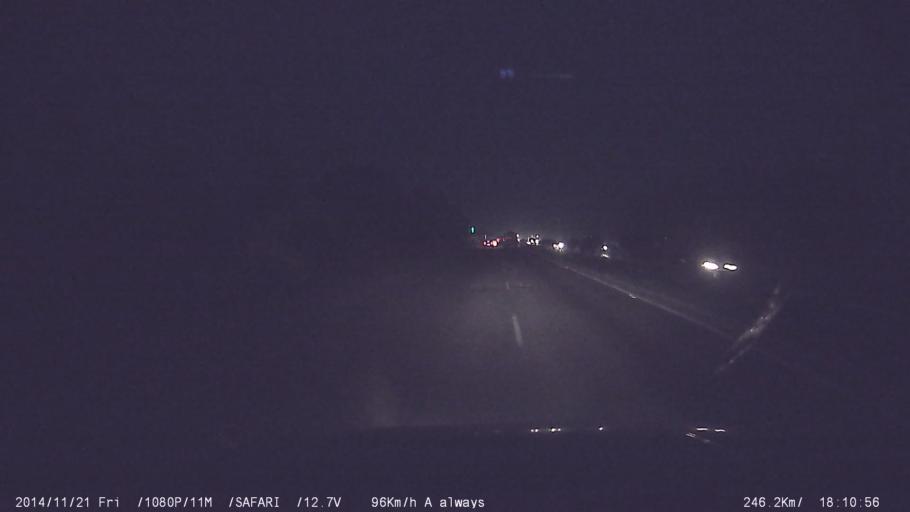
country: IN
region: Tamil Nadu
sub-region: Kancheepuram
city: Kanchipuram
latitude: 12.8984
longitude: 79.5547
